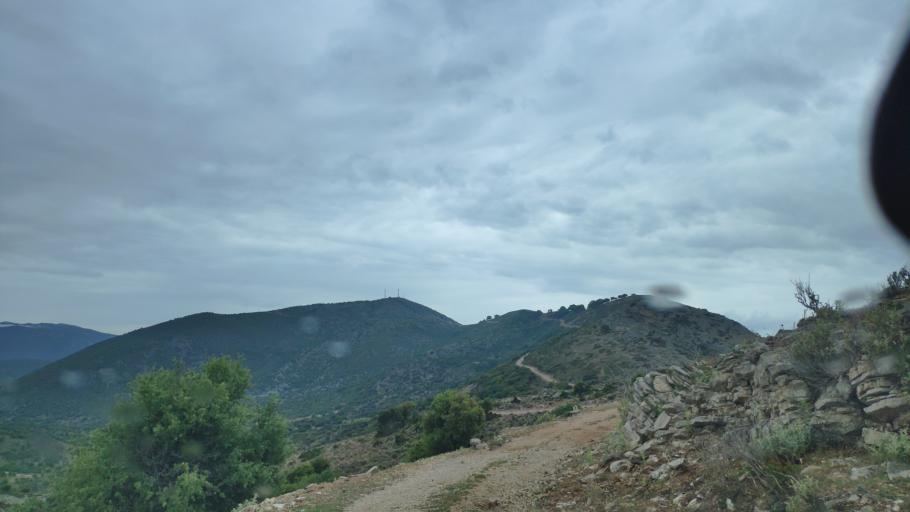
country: GR
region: West Greece
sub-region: Nomos Aitolias kai Akarnanias
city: Archontochorion
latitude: 38.6792
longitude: 21.0175
